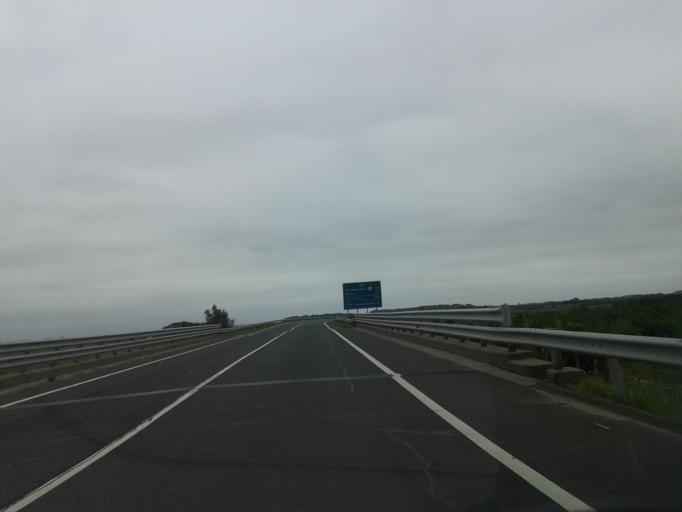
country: HU
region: Bacs-Kiskun
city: Dunavecse
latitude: 46.9345
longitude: 18.9854
